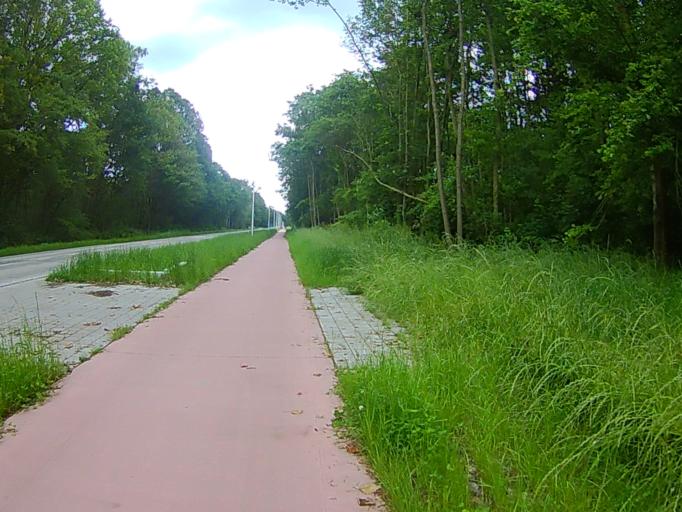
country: BE
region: Flanders
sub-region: Provincie Antwerpen
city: Berlaar
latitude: 51.1326
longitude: 4.6382
